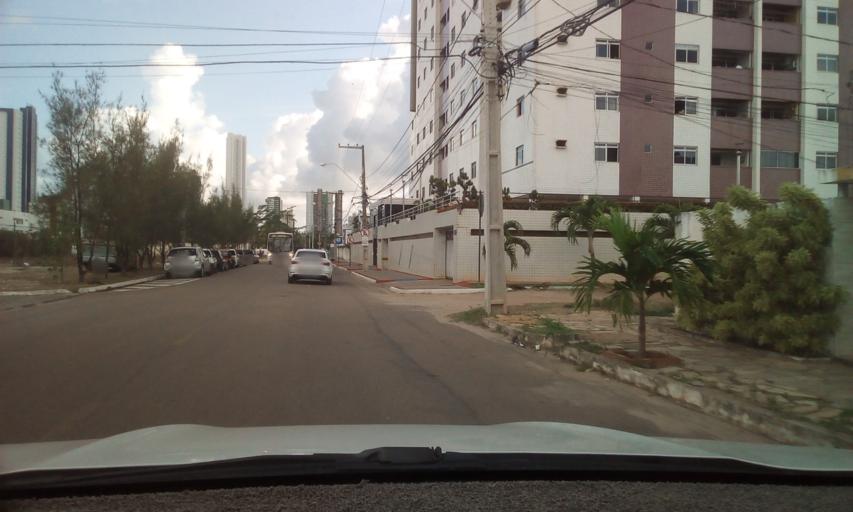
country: BR
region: Paraiba
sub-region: Joao Pessoa
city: Joao Pessoa
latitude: -7.0739
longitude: -34.8431
